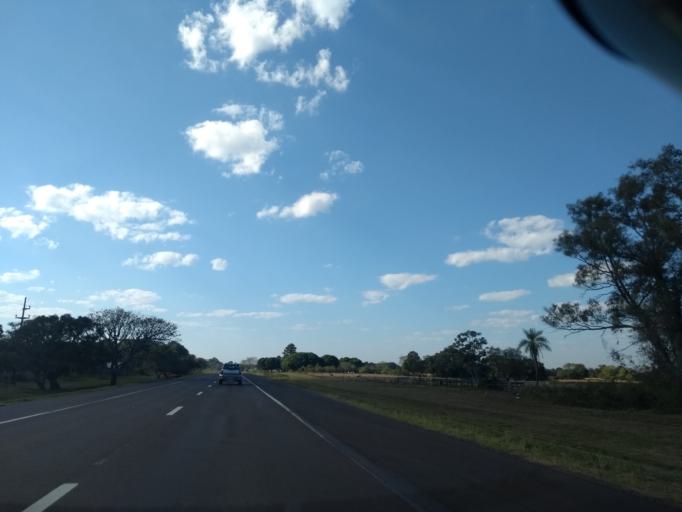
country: AR
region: Corrientes
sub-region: Departamento de San Cosme
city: San Cosme
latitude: -27.3662
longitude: -58.4322
